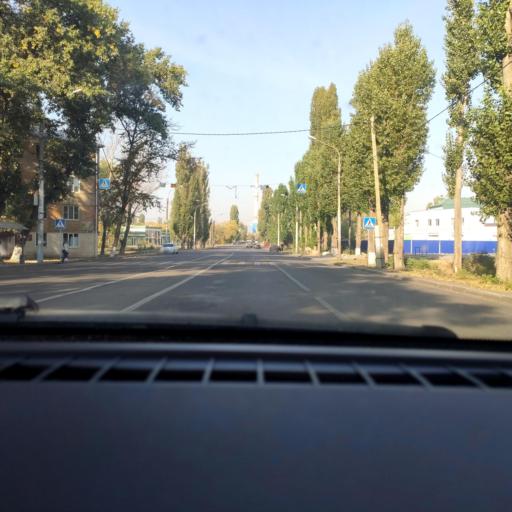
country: RU
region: Voronezj
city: Maslovka
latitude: 51.6221
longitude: 39.2400
